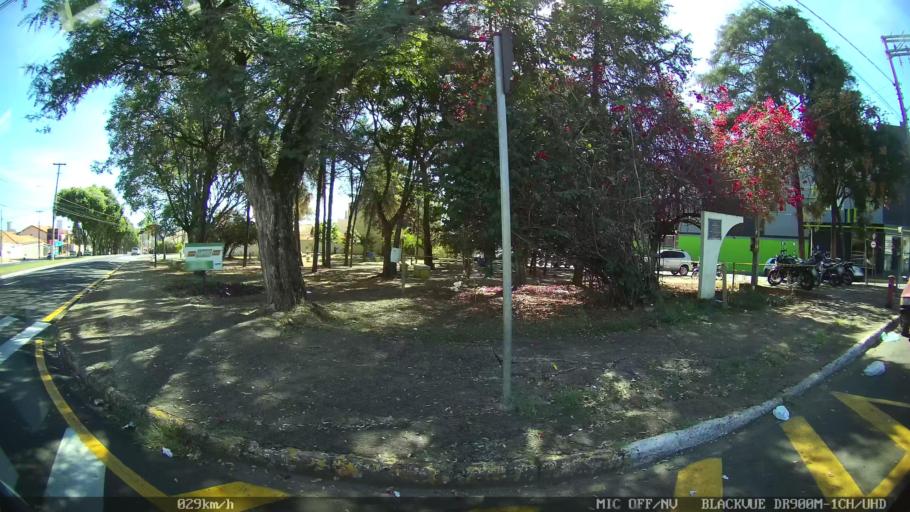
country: BR
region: Sao Paulo
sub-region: Franca
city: Franca
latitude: -20.5601
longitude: -47.4016
